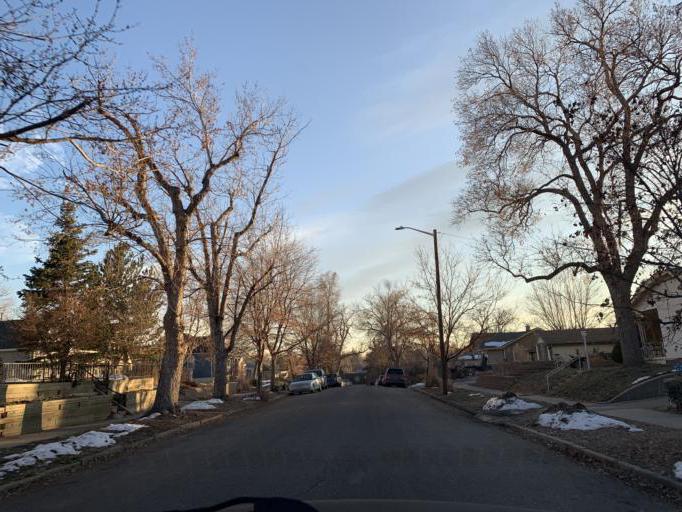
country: US
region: Colorado
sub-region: Adams County
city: Berkley
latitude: 39.7851
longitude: -105.0381
